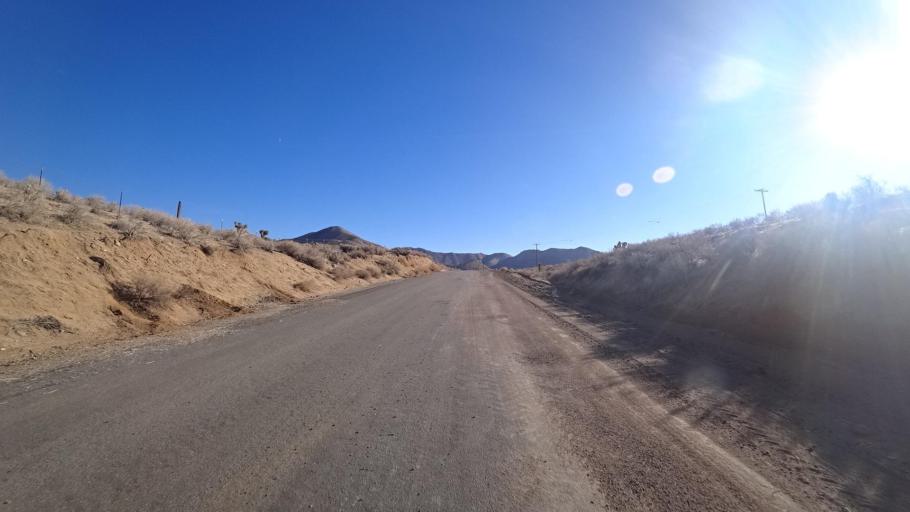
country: US
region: California
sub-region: Kern County
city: Weldon
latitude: 35.6043
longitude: -118.2425
